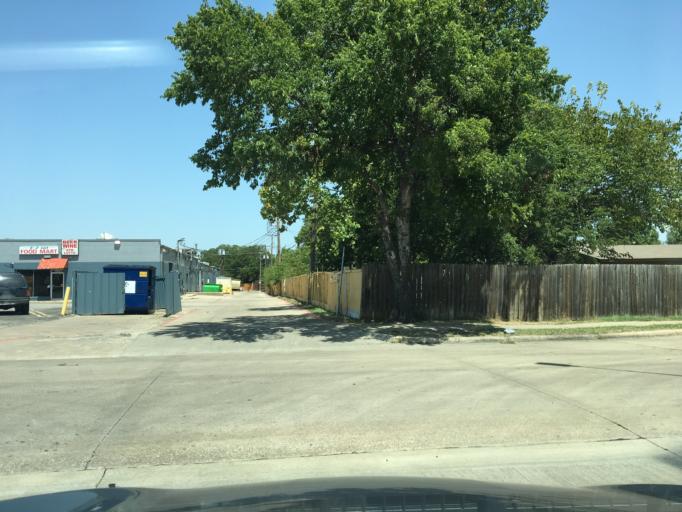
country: US
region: Texas
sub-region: Dallas County
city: Garland
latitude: 32.8976
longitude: -96.6296
